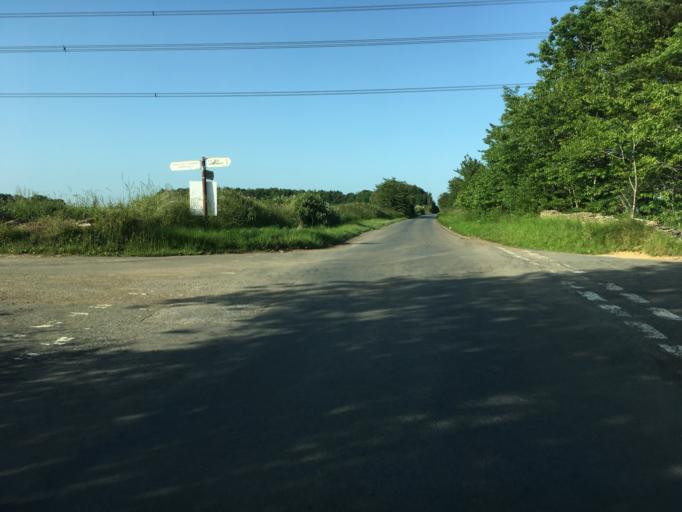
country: GB
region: England
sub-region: Gloucestershire
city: Lechlade
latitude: 51.7717
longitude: -1.7083
